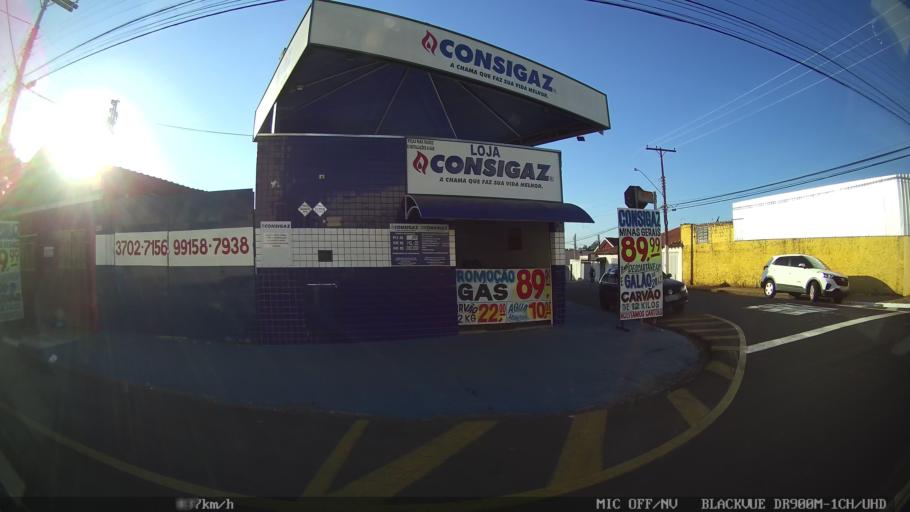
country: BR
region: Sao Paulo
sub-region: Franca
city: Franca
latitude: -20.5254
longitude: -47.3794
